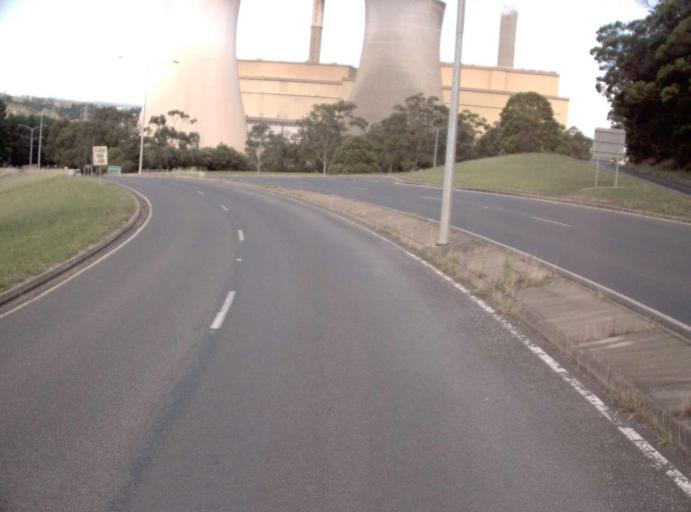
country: AU
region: Victoria
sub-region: Latrobe
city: Moe
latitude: -38.1784
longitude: 146.3345
